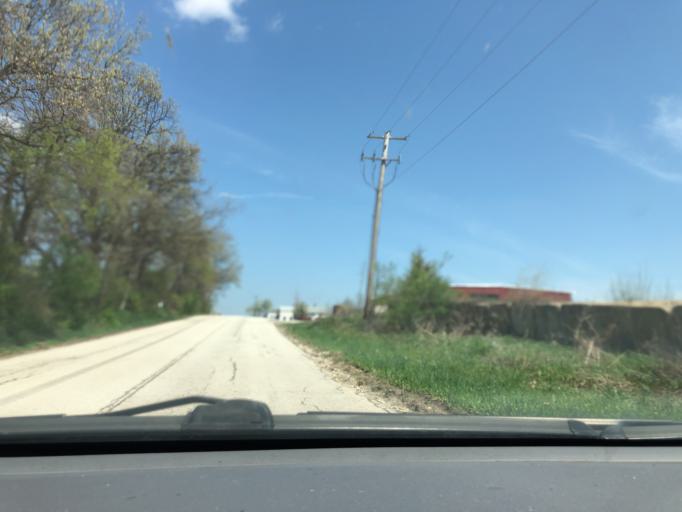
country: US
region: Illinois
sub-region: Kane County
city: Hampshire
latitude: 42.0961
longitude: -88.4815
